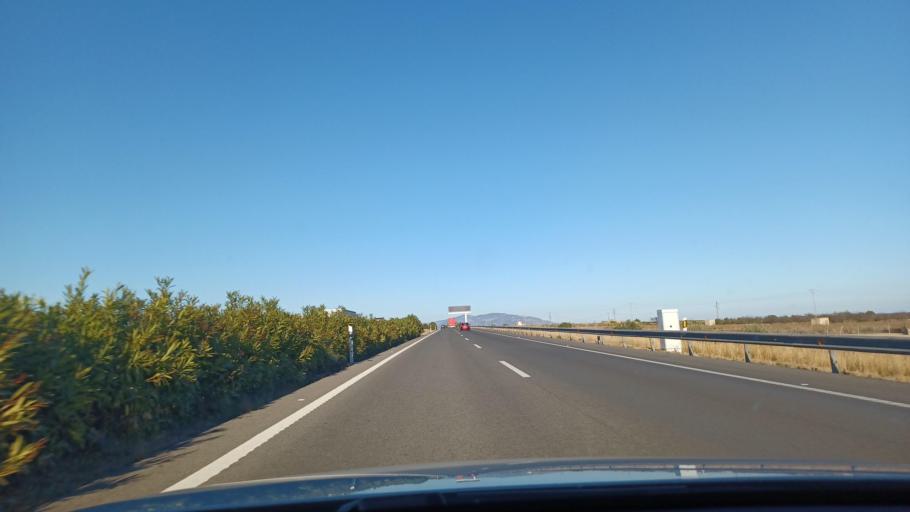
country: ES
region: Valencia
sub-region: Provincia de Castello
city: Orpesa/Oropesa del Mar
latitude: 40.1554
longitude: 0.1518
